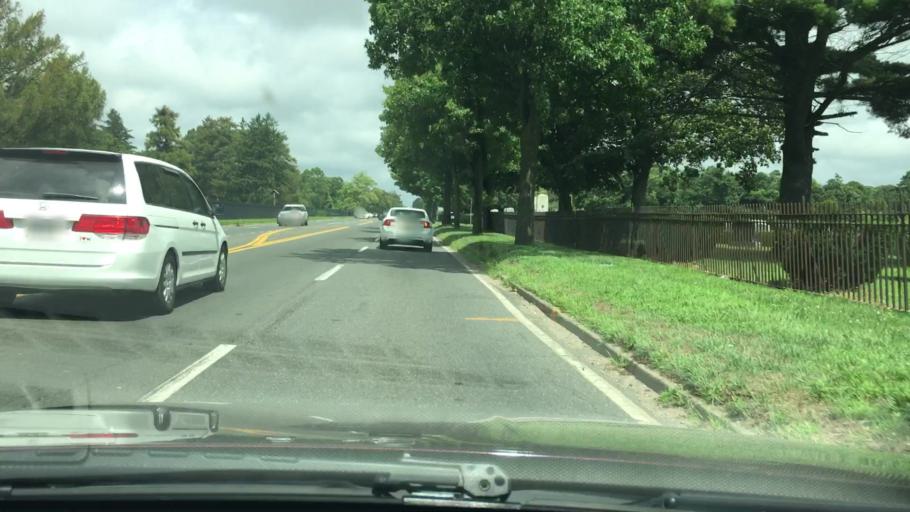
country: US
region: New York
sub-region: Suffolk County
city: East Farmingdale
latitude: 40.7367
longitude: -73.3993
